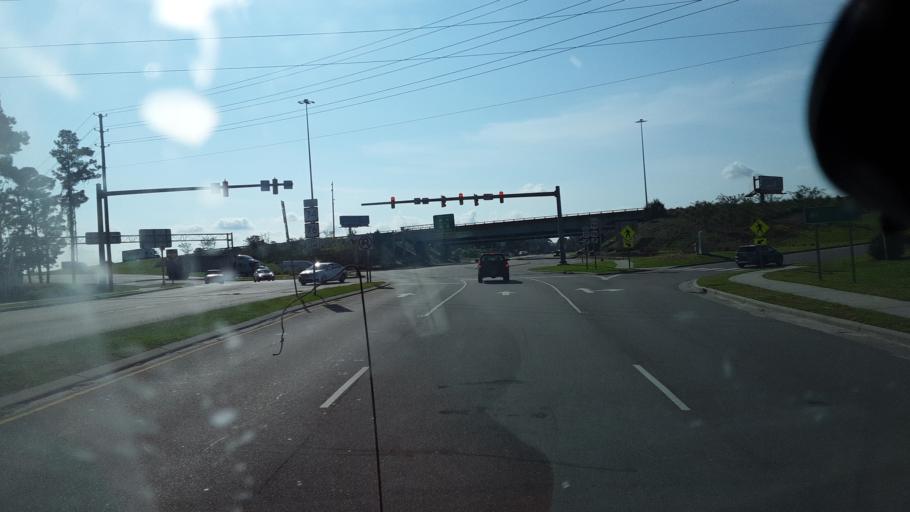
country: US
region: North Carolina
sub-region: Brunswick County
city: Navassa
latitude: 34.2331
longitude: -77.9957
